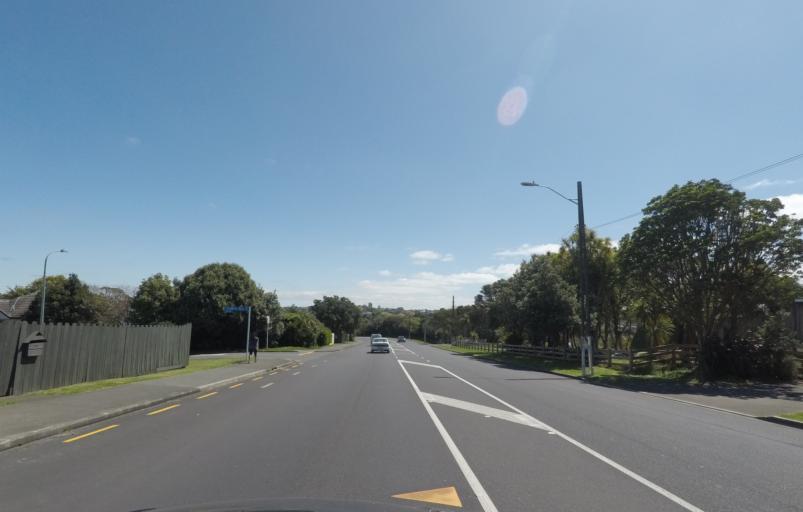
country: NZ
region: Auckland
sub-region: Auckland
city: Tamaki
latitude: -36.8873
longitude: 174.8264
